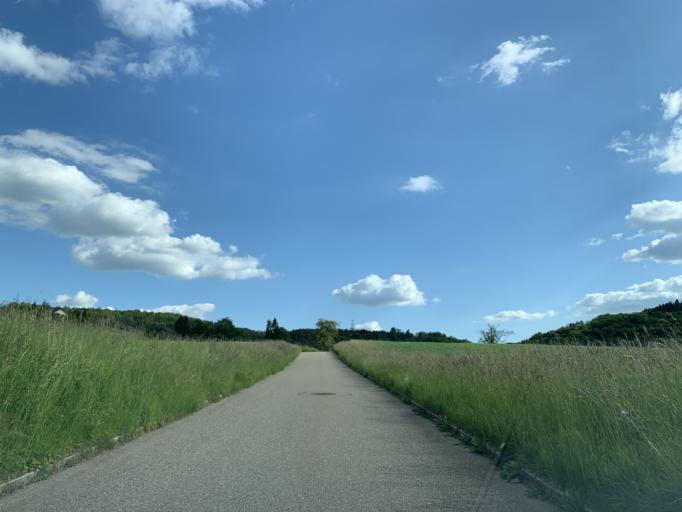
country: CH
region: Zurich
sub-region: Bezirk Winterthur
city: Wuelflingen (Kreis 6) / Niederfeld
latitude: 47.4994
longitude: 8.6749
